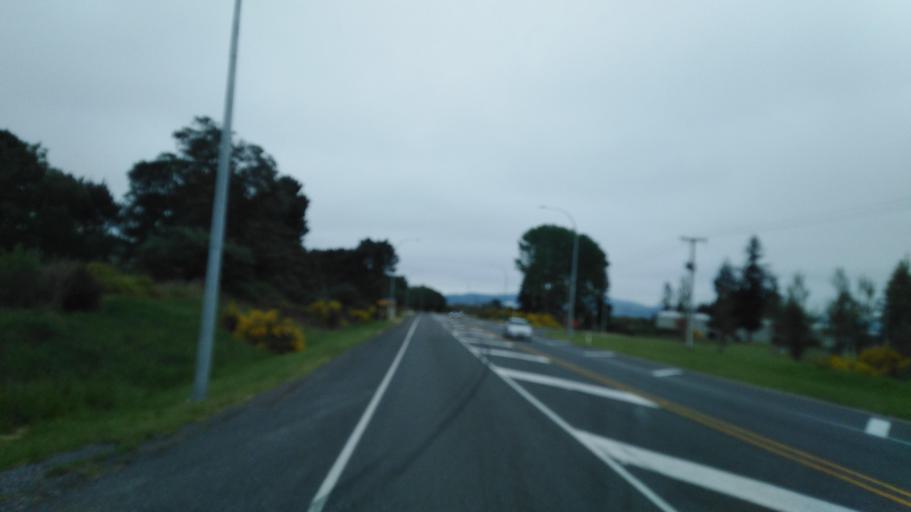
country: NZ
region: Waikato
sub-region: Taupo District
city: Taupo
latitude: -38.7053
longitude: 176.1081
